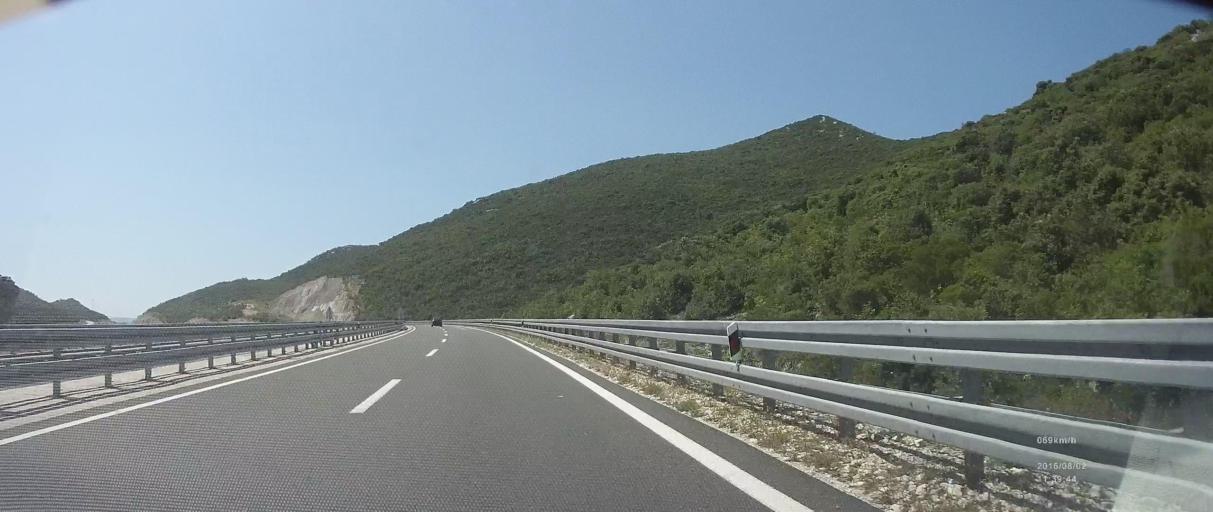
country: HR
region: Dubrovacko-Neretvanska
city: Komin
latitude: 43.0829
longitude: 17.4903
